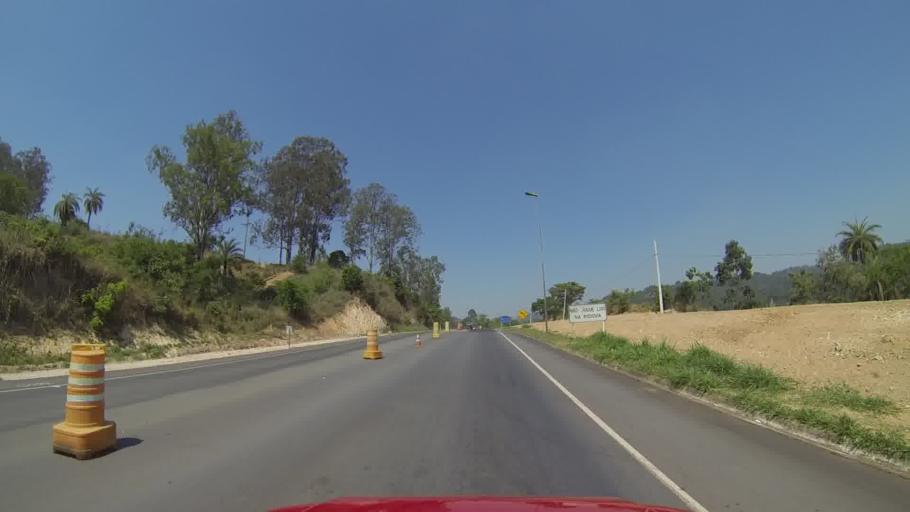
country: BR
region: Minas Gerais
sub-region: Mateus Leme
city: Mateus Leme
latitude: -20.0198
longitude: -44.4969
